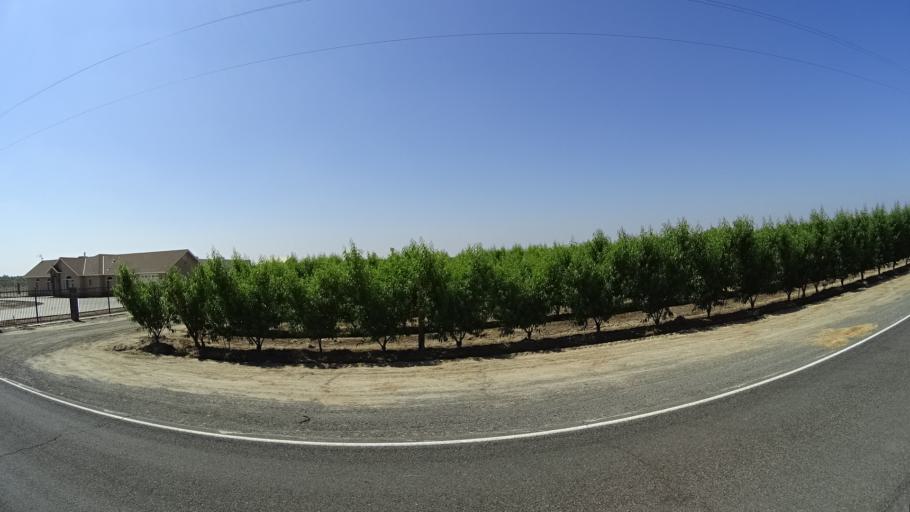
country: US
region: California
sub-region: Fresno County
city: Kingsburg
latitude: 36.4524
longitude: -119.5966
